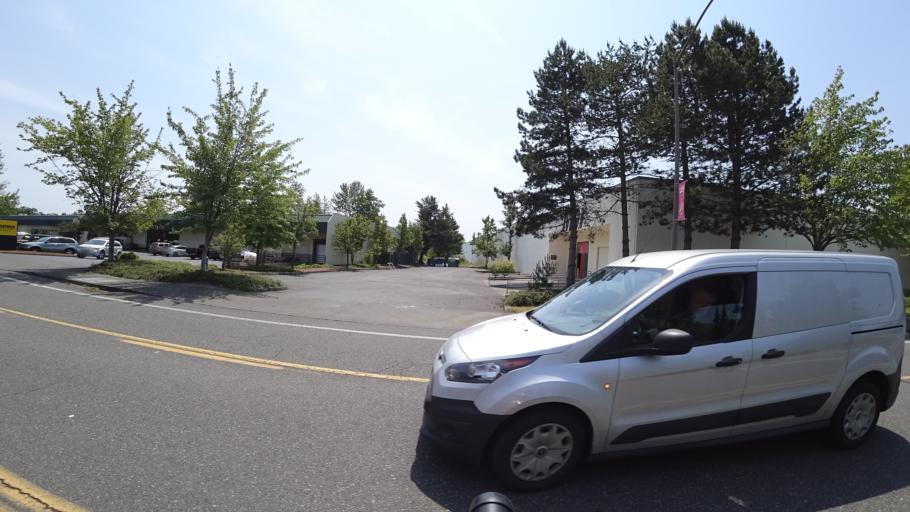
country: US
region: Washington
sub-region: Clark County
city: Vancouver
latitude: 45.5966
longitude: -122.6771
